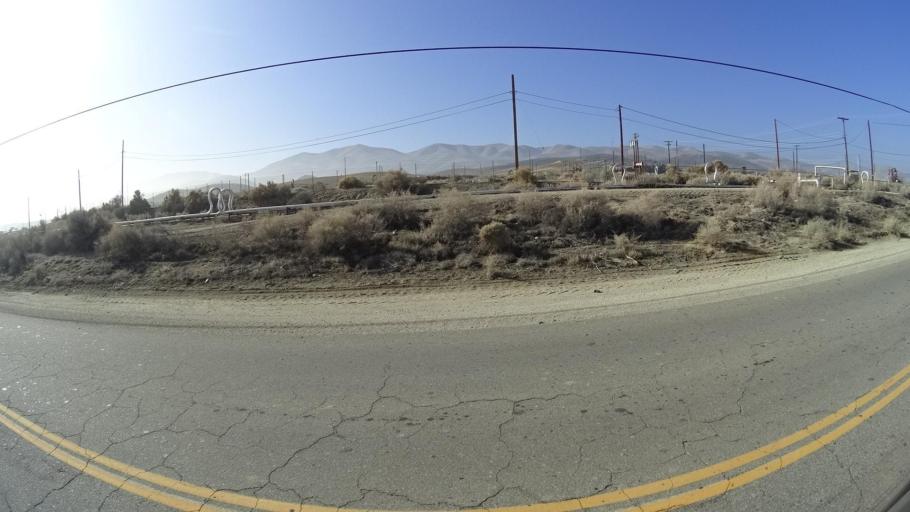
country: US
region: California
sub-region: Kern County
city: Taft Heights
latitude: 35.2029
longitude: -119.5944
